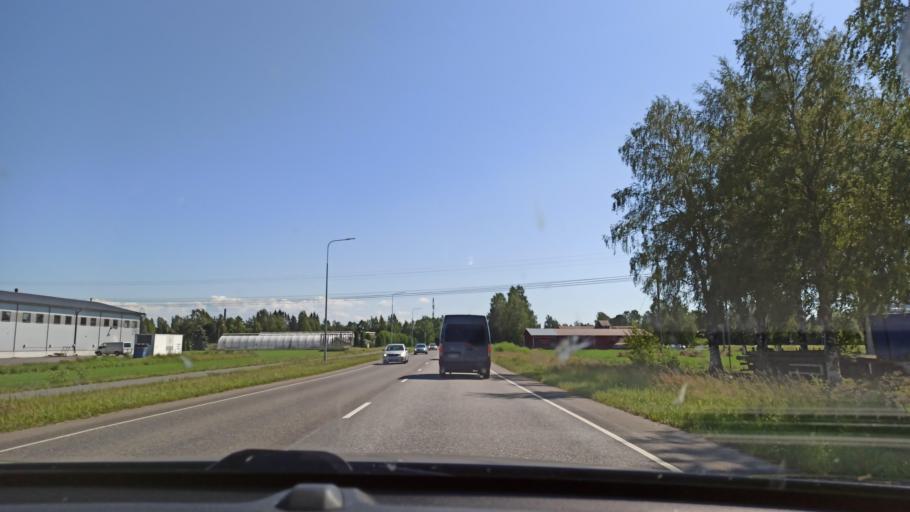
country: FI
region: Satakunta
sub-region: Pori
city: Pori
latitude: 61.5096
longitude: 21.8034
